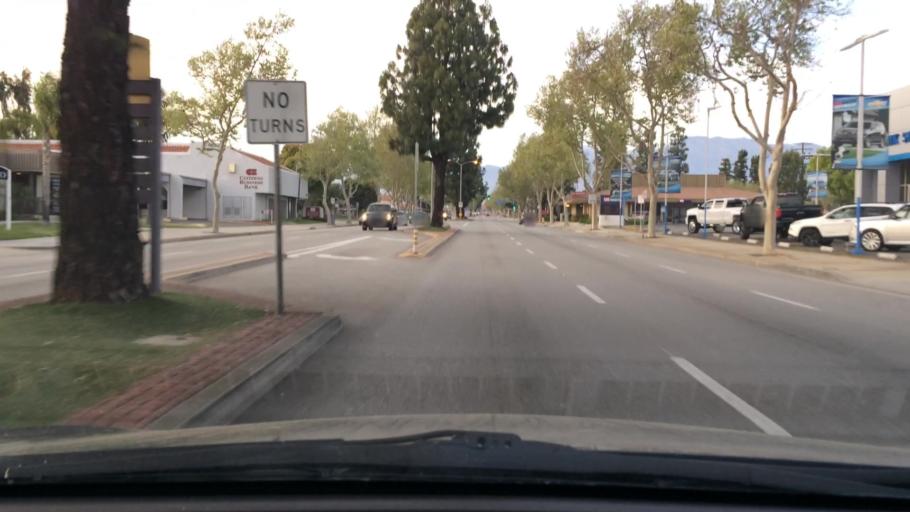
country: US
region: California
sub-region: San Bernardino County
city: Chino
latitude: 34.0198
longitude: -117.6893
